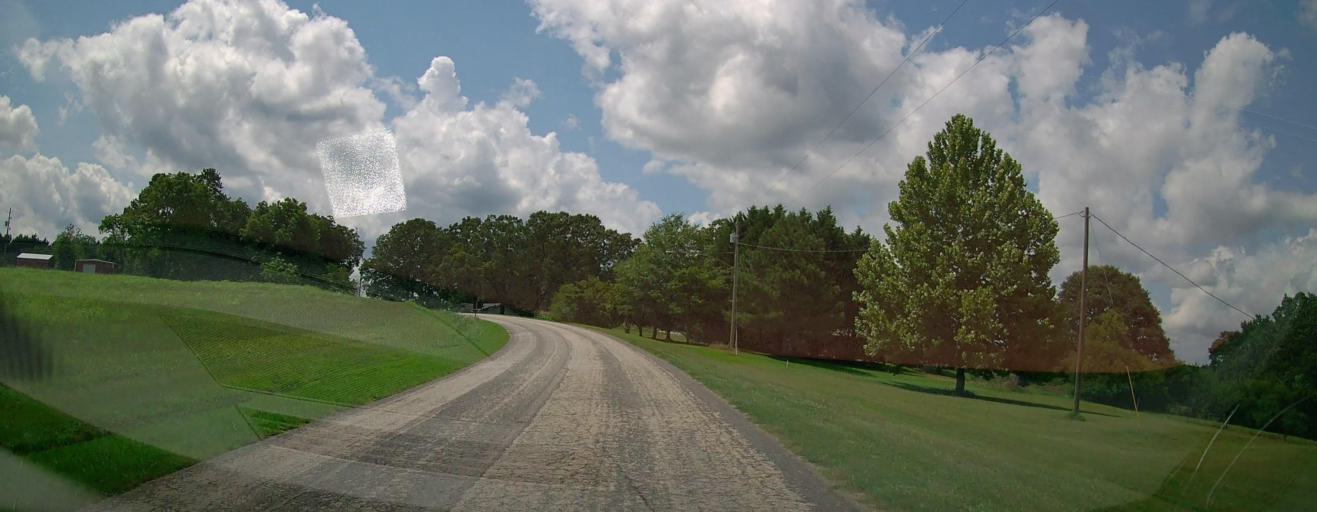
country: US
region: Georgia
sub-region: Carroll County
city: Bowdon
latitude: 33.5130
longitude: -85.3410
